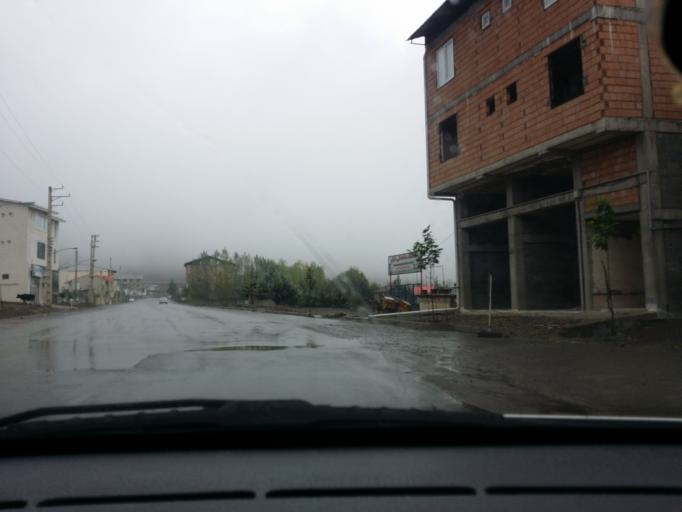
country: IR
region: Mazandaran
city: Chalus
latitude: 36.5232
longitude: 51.2337
